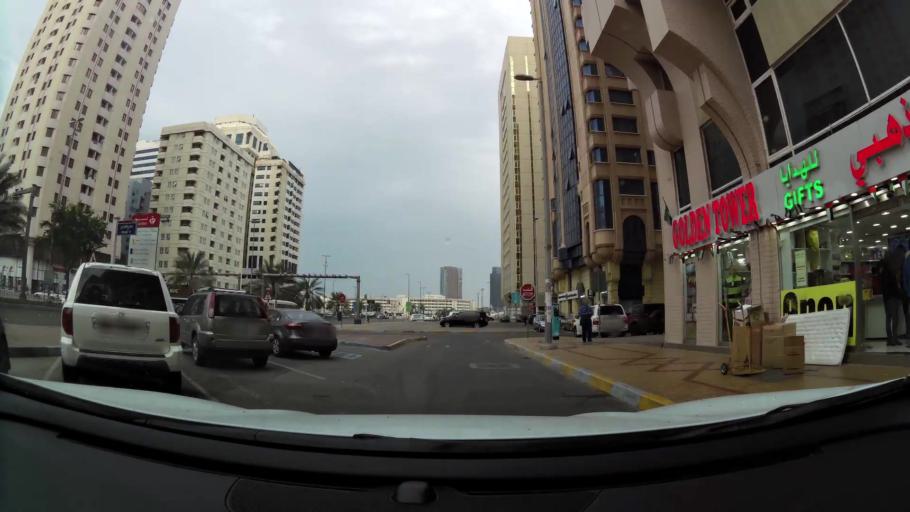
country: AE
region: Abu Dhabi
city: Abu Dhabi
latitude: 24.4959
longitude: 54.3777
